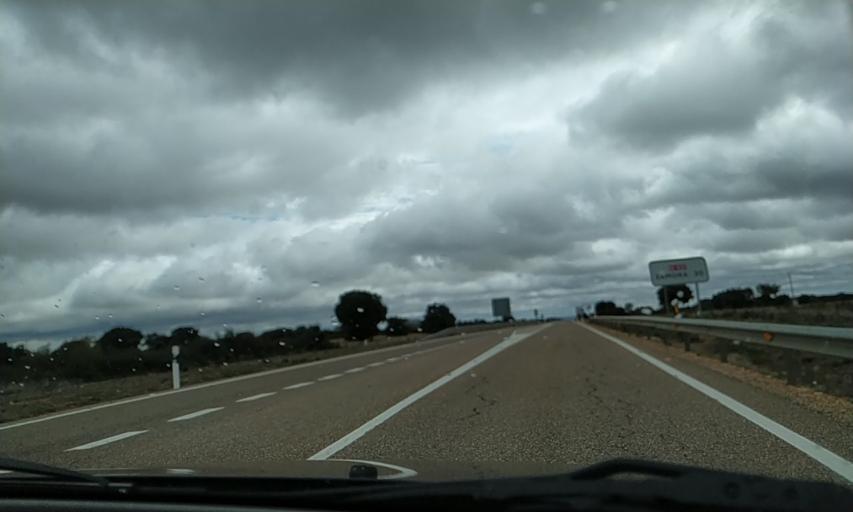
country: ES
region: Castille and Leon
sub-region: Provincia de Zamora
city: Perilla de Castro
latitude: 41.7347
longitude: -5.8268
